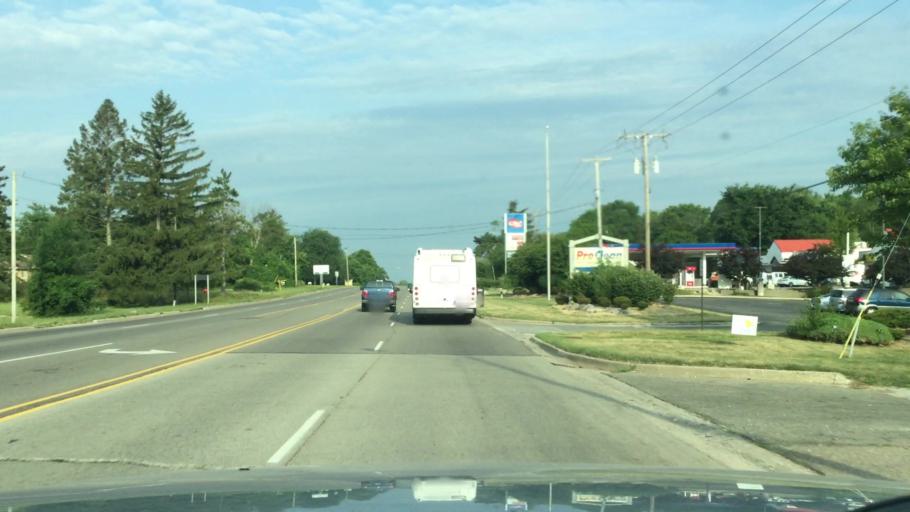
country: US
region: Michigan
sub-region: Genesee County
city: Flushing
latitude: 43.0606
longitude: -83.7734
